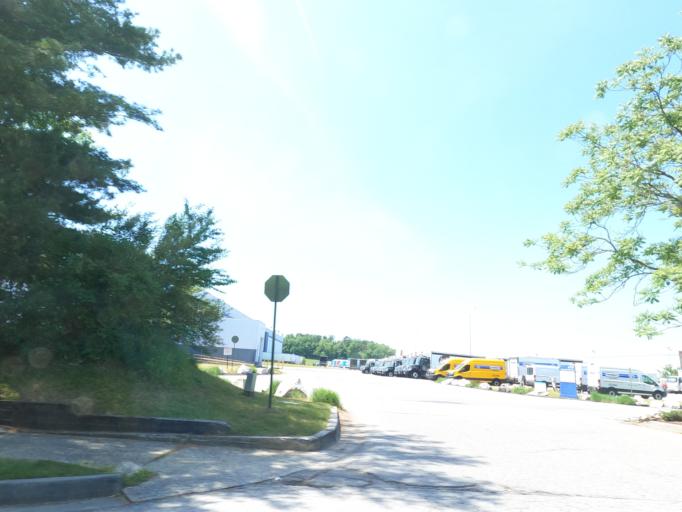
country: US
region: Maryland
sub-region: Howard County
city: Savage
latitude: 39.1852
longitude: -76.8098
